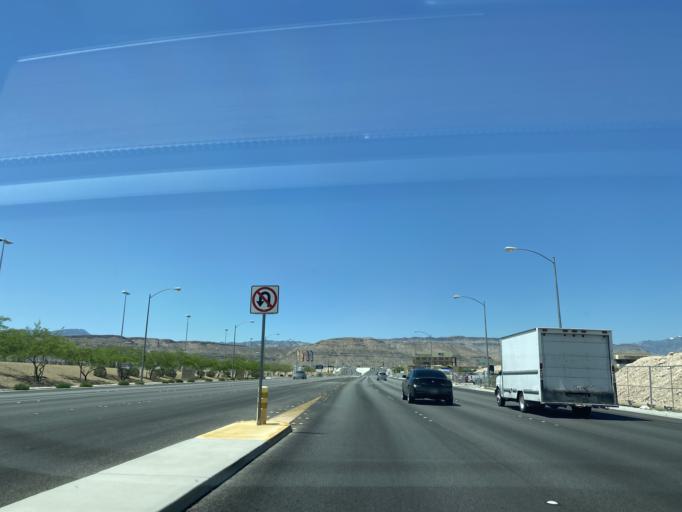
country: US
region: Nevada
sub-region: Clark County
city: Spring Valley
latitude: 36.0705
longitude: -115.2807
